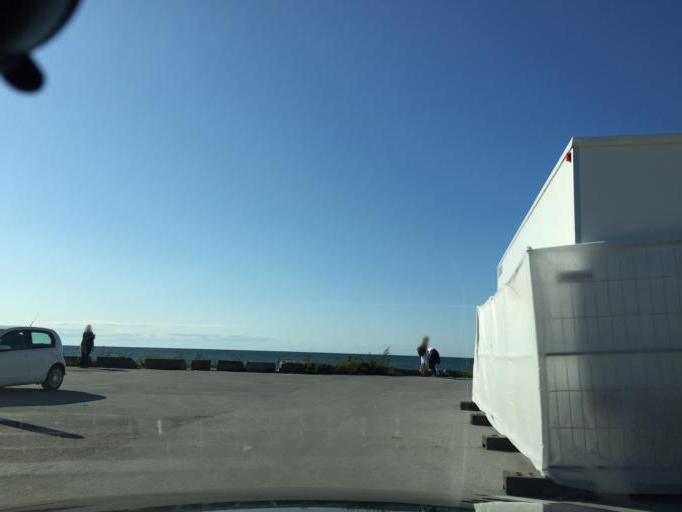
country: SE
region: Gotland
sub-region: Gotland
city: Visby
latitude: 57.6402
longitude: 18.2867
